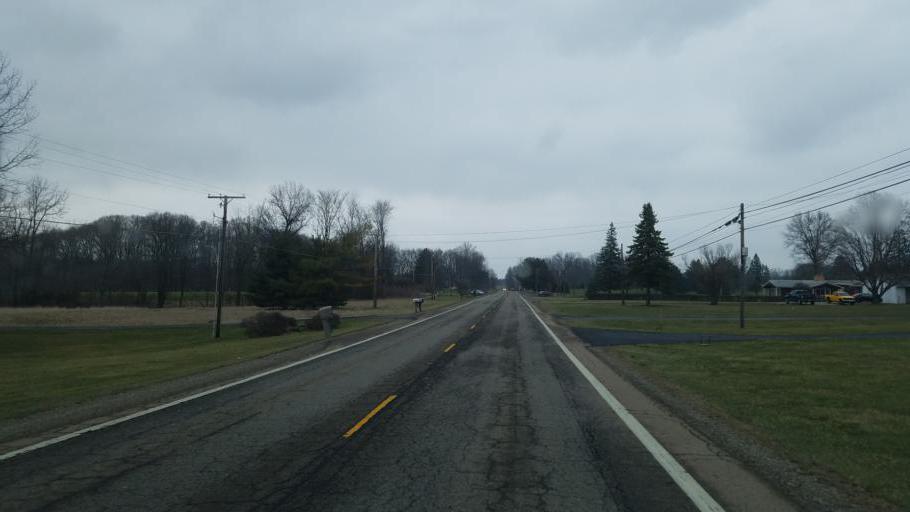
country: US
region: Ohio
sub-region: Crawford County
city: Galion
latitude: 40.7062
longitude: -82.8152
